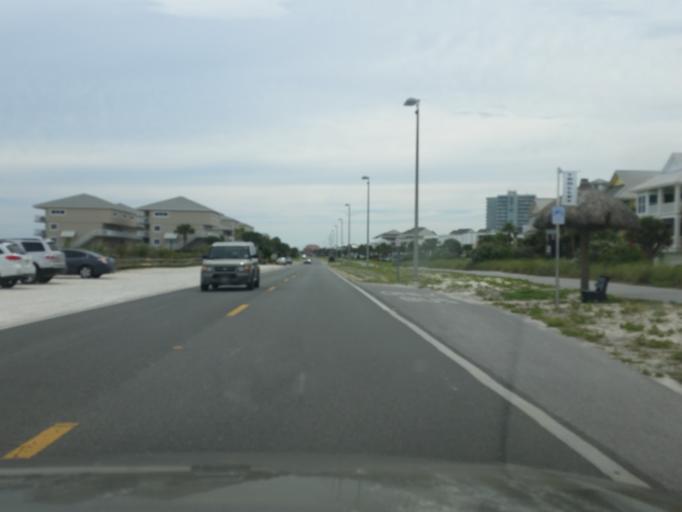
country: US
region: Florida
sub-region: Santa Rosa County
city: Gulf Breeze
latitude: 30.3275
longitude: -87.1676
